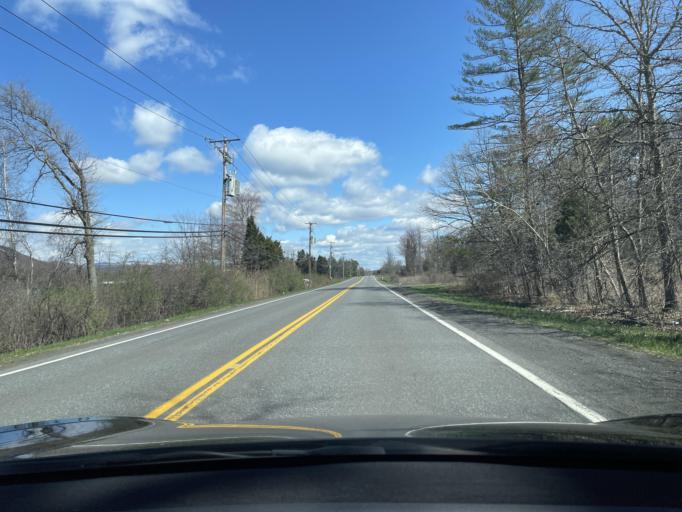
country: US
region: New York
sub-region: Ulster County
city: Glasco
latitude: 42.0436
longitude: -73.9809
